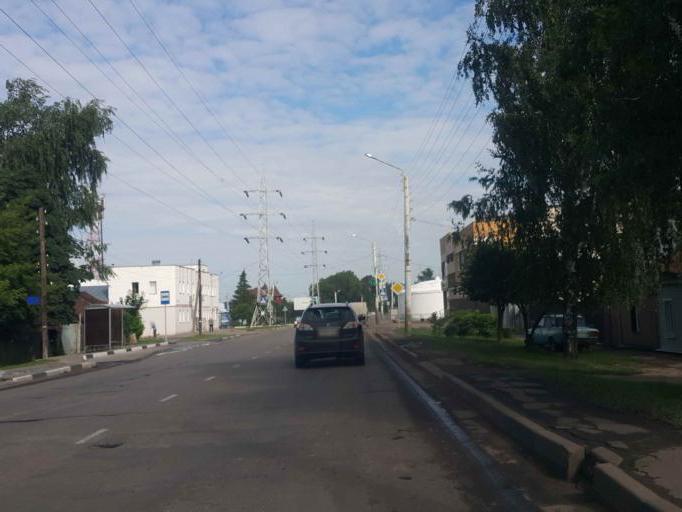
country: RU
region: Tambov
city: Pokrovo-Prigorodnoye
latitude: 52.7085
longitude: 41.4197
